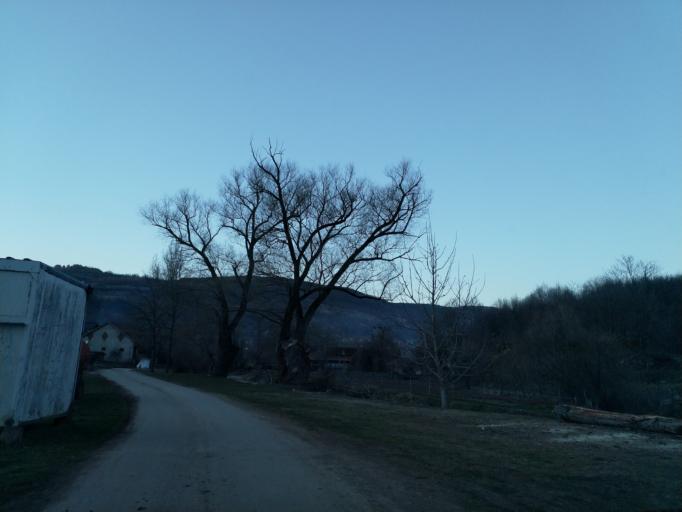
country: RS
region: Central Serbia
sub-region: Pomoravski Okrug
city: Paracin
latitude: 43.9301
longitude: 21.5211
